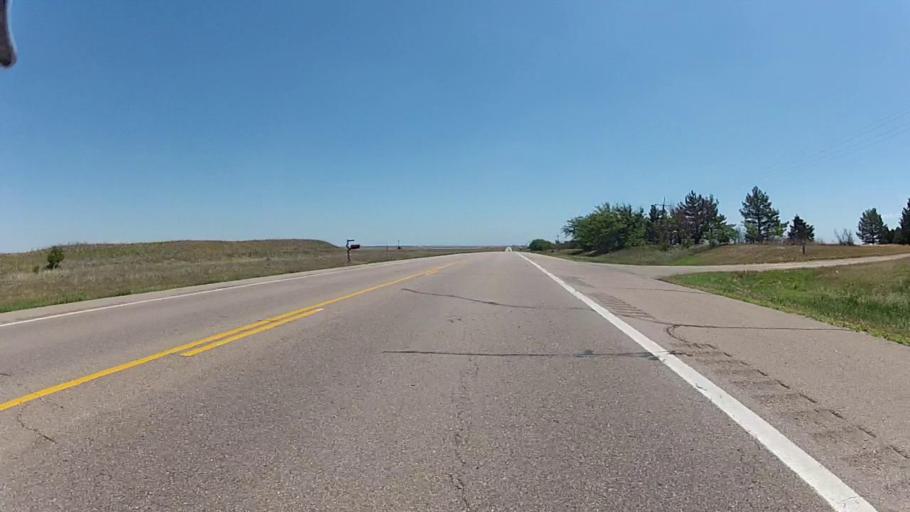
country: US
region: Kansas
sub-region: Ford County
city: Dodge City
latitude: 37.7078
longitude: -100.1278
